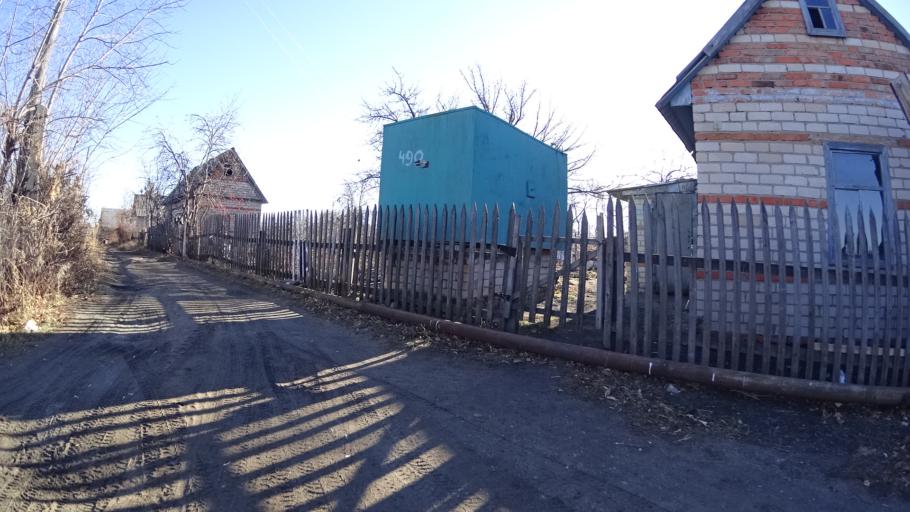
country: RU
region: Chelyabinsk
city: Troitsk
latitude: 54.0818
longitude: 61.5099
